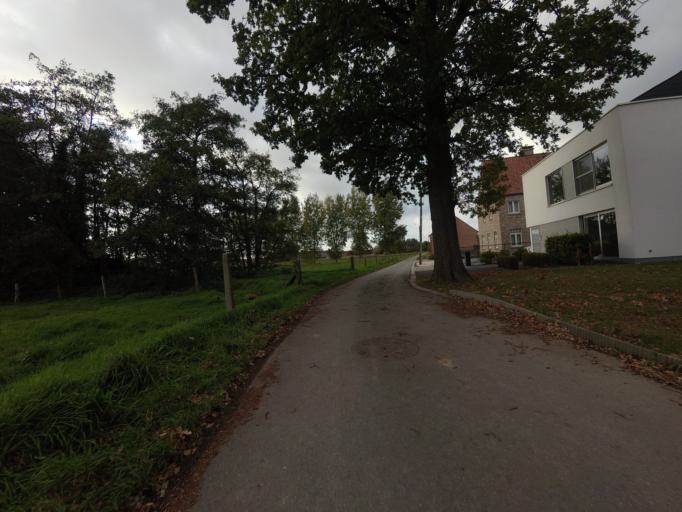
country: BE
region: Flanders
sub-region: Provincie Vlaams-Brabant
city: Zemst
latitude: 50.9675
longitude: 4.4383
